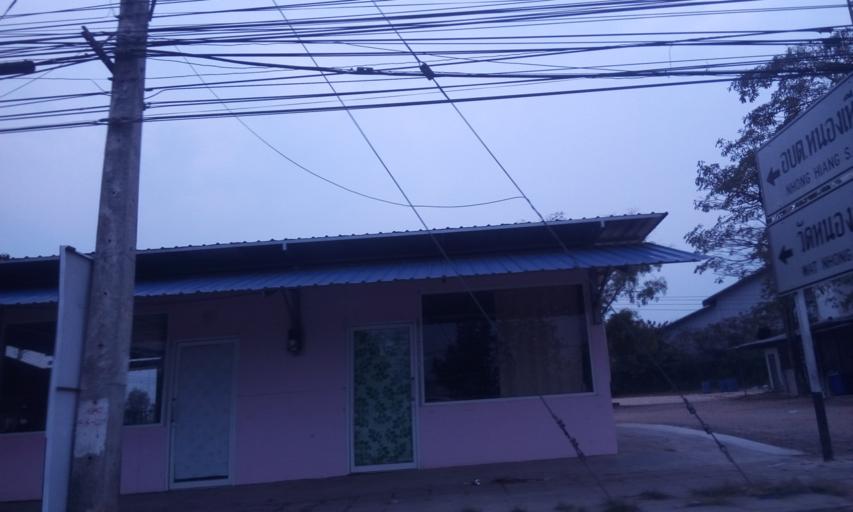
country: TH
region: Chon Buri
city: Ko Chan
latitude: 13.4847
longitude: 101.2786
